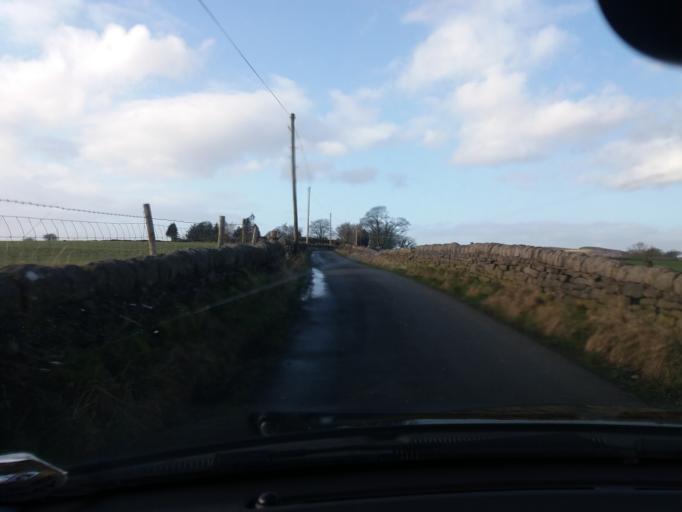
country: GB
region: England
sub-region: Lancashire
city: Adlington
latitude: 53.6346
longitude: -2.5811
